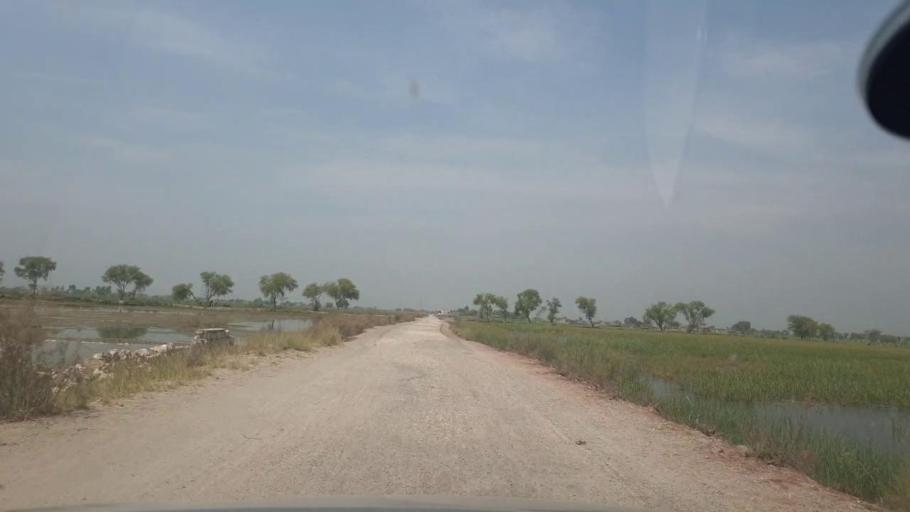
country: PK
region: Sindh
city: Thul
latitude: 28.1692
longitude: 68.6341
